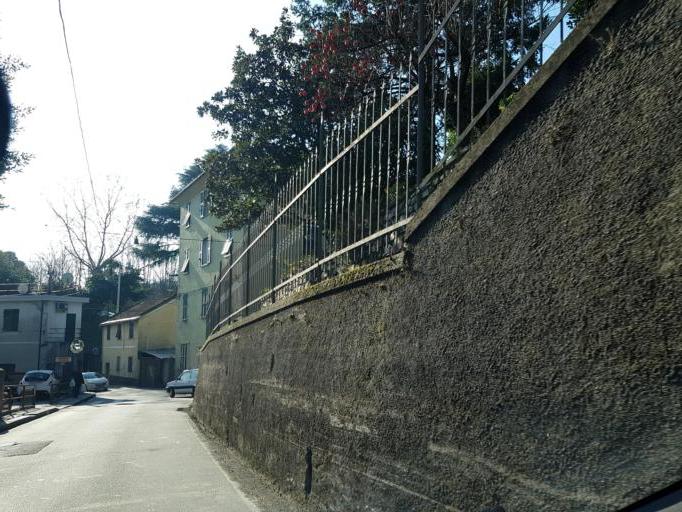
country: IT
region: Liguria
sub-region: Provincia di Genova
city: Santa Marta
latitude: 44.5004
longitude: 8.9002
